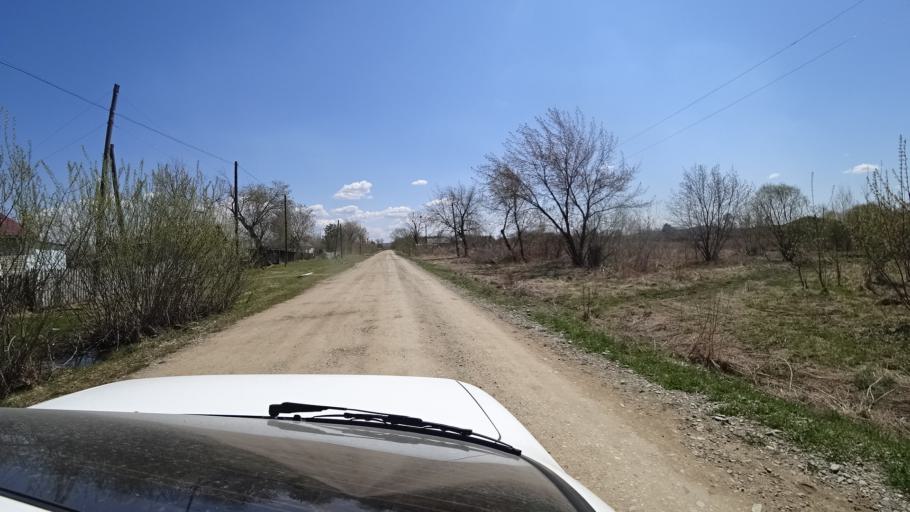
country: RU
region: Primorskiy
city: Dal'nerechensk
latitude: 45.8010
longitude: 133.7656
